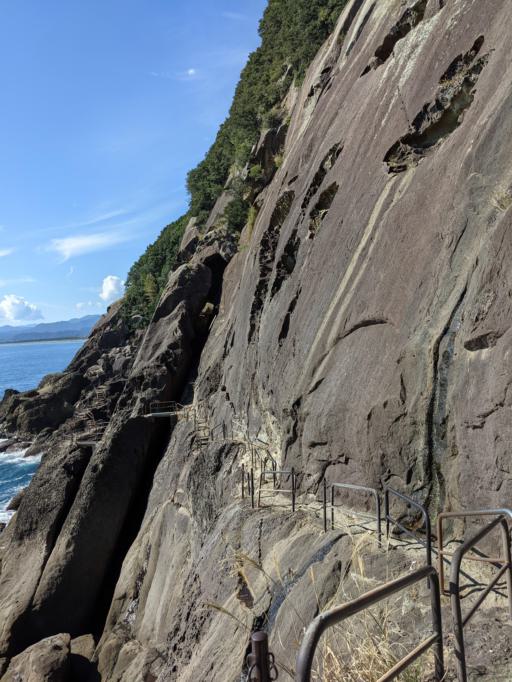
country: JP
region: Mie
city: Owase
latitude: 33.8902
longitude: 136.1157
